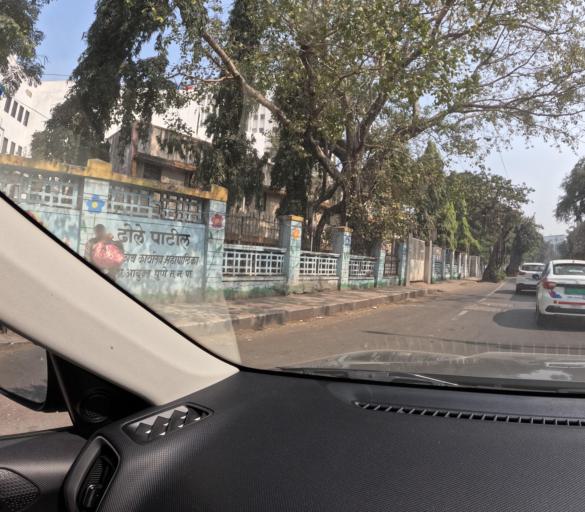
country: IN
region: Maharashtra
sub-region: Pune Division
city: Pune
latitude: 18.5253
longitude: 73.8680
